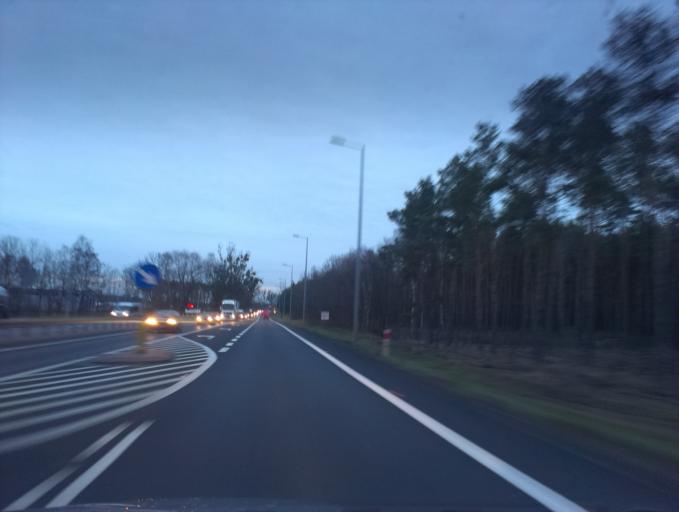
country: PL
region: Greater Poland Voivodeship
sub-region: Powiat poznanski
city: Zlotniki
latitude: 52.5298
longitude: 16.8341
